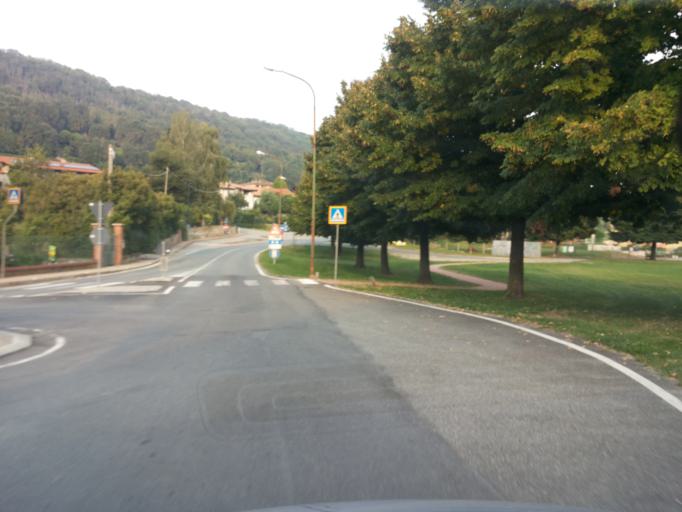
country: IT
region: Piedmont
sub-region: Provincia di Torino
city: Piverone
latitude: 45.4482
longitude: 8.0079
